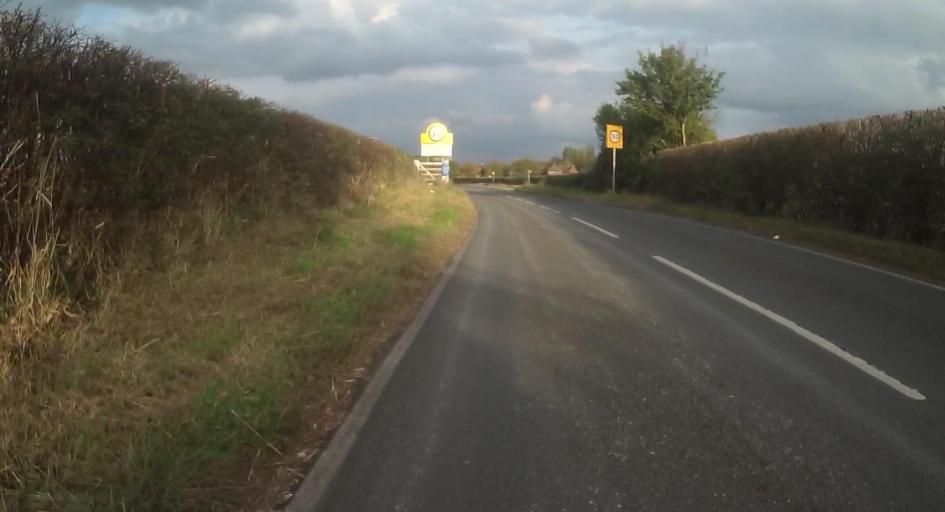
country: GB
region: England
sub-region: Hampshire
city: Tadley
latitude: 51.3832
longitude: -1.1599
